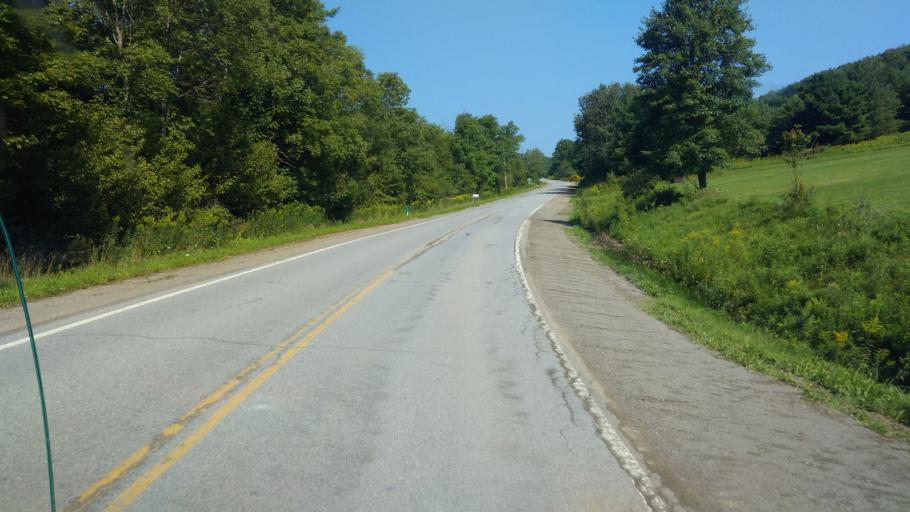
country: US
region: New York
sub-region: Allegany County
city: Bolivar
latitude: 42.0952
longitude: -78.1726
